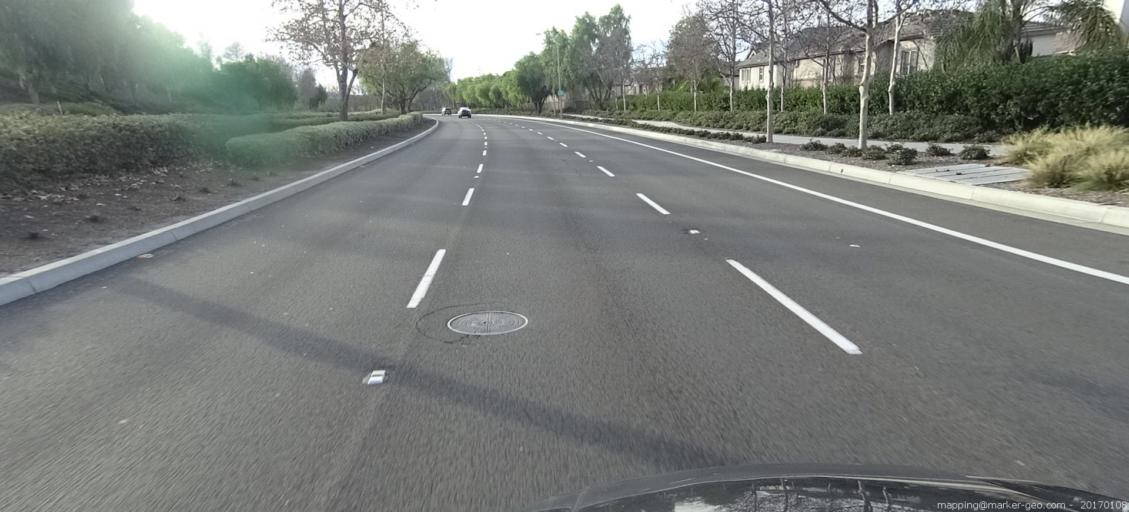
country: US
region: California
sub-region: Orange County
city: Ladera Ranch
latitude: 33.5674
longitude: -117.6351
